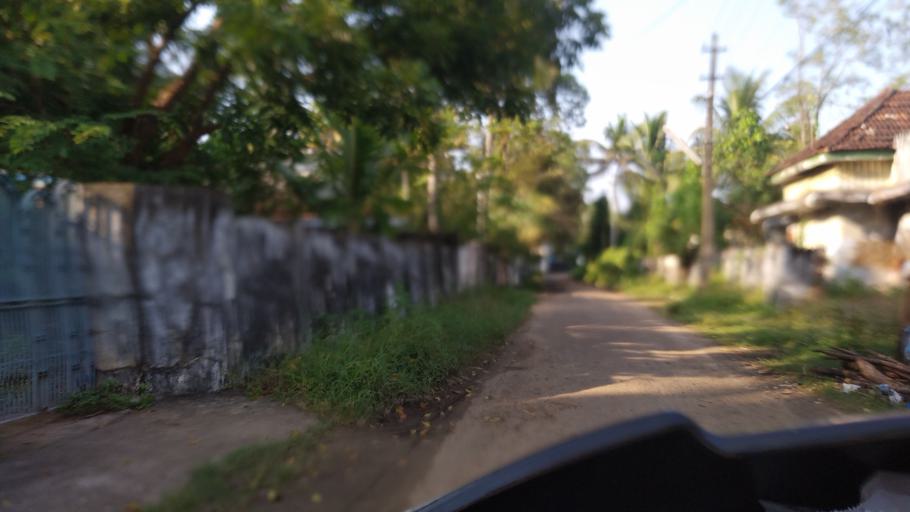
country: IN
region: Kerala
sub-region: Ernakulam
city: Elur
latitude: 10.0461
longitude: 76.2263
